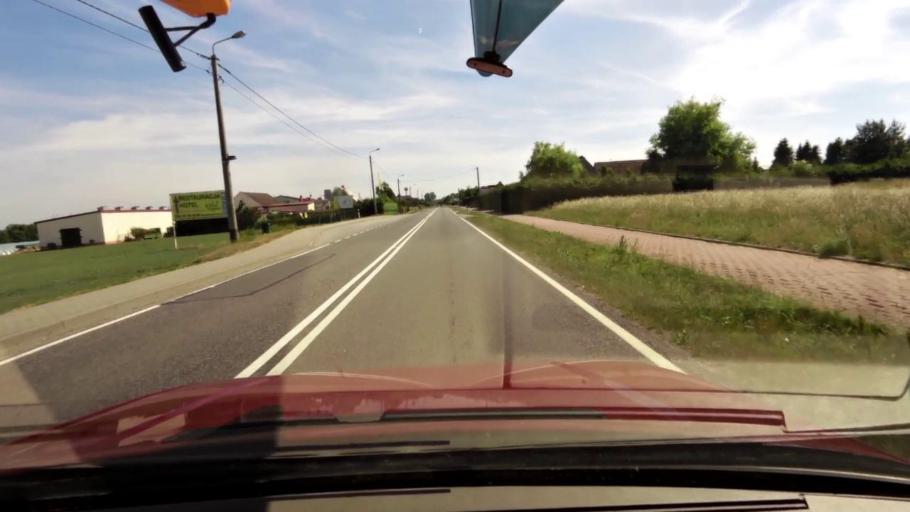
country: PL
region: Pomeranian Voivodeship
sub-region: Powiat slupski
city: Kobylnica
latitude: 54.4189
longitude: 17.0074
